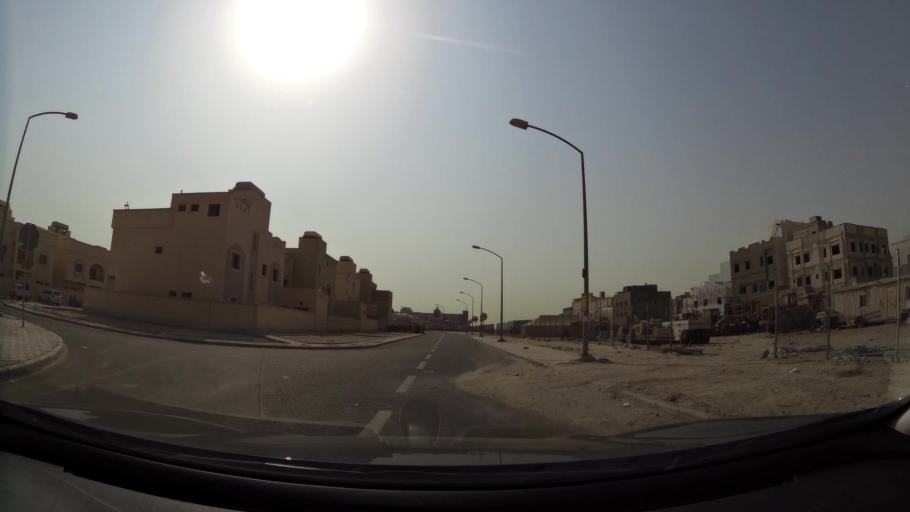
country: KW
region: Muhafazat al Jahra'
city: Al Jahra'
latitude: 29.3489
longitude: 47.7531
